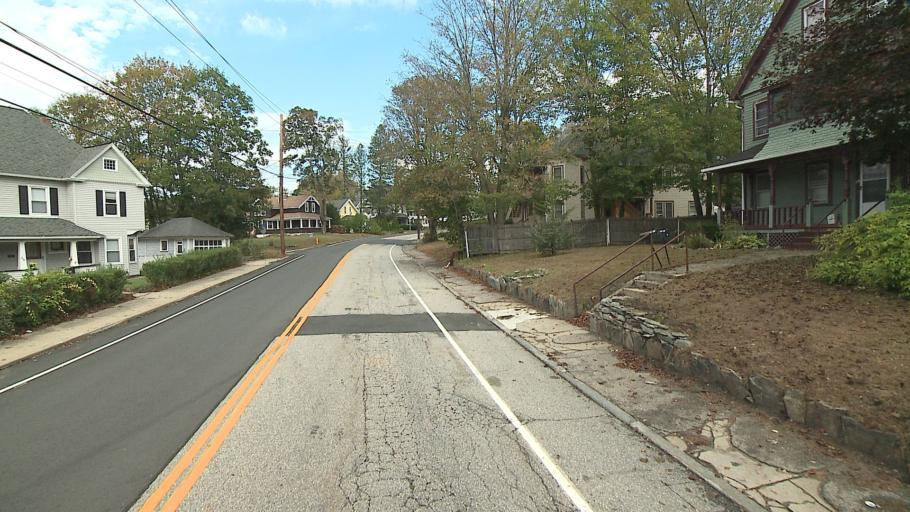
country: US
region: Connecticut
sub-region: Windham County
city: Putnam
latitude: 41.9250
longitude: -71.9000
